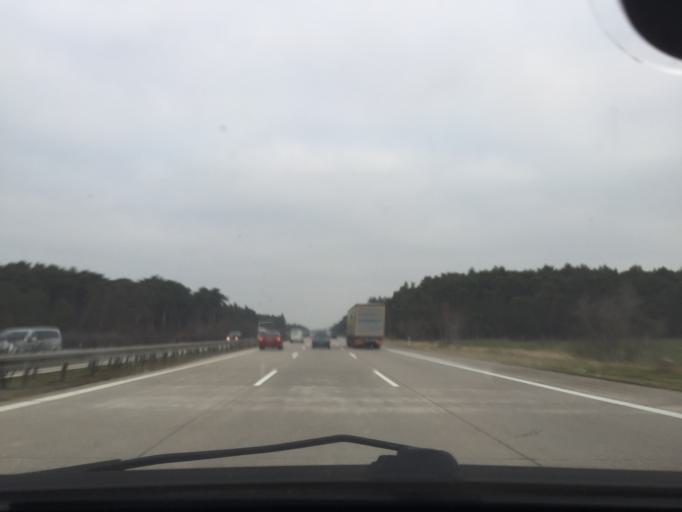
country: DE
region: Brandenburg
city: Wollin
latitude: 52.2983
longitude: 12.4690
